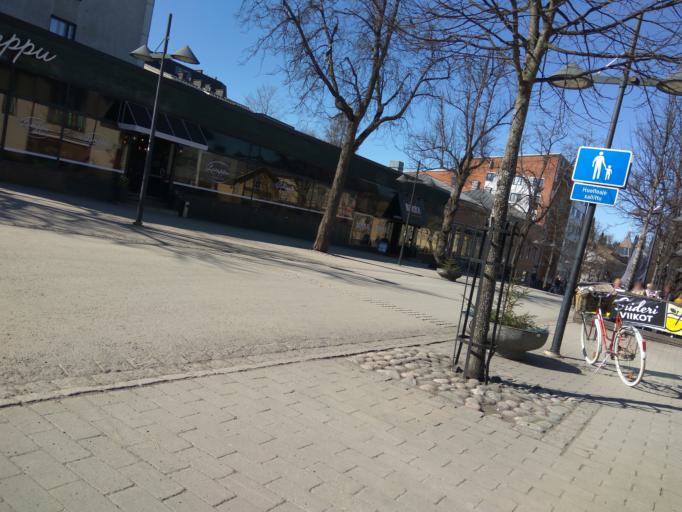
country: FI
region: South Karelia
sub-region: Lappeenranta
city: Lappeenranta
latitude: 61.0598
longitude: 28.1854
